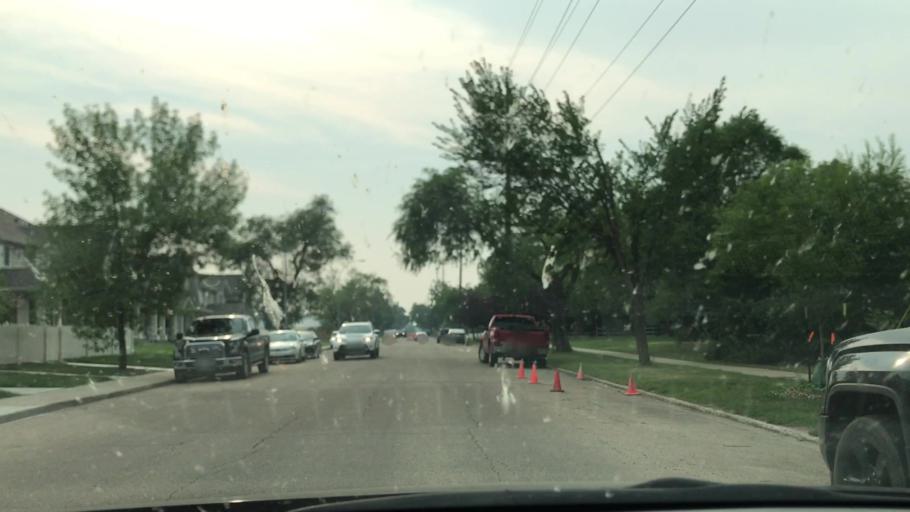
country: CA
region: Alberta
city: Edmonton
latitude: 53.5922
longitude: -113.5463
